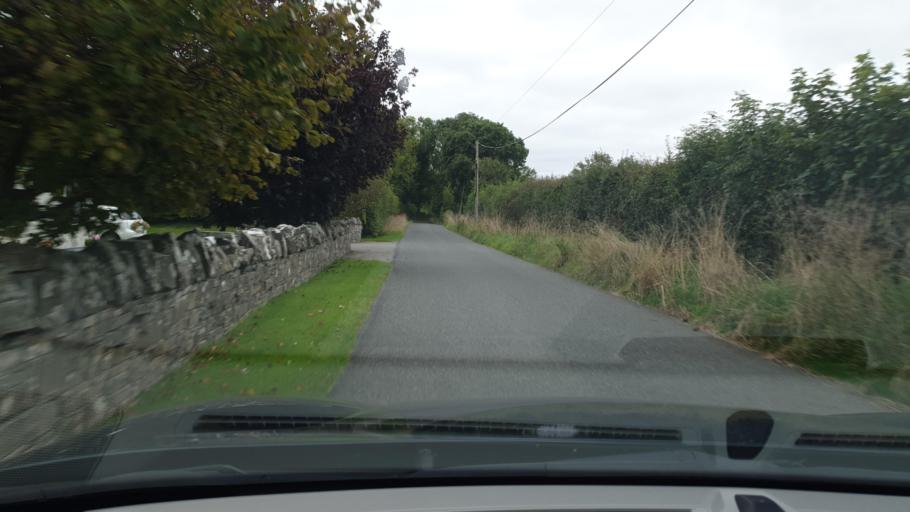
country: IE
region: Leinster
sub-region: An Mhi
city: Dunshaughlin
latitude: 53.4889
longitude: -6.5941
